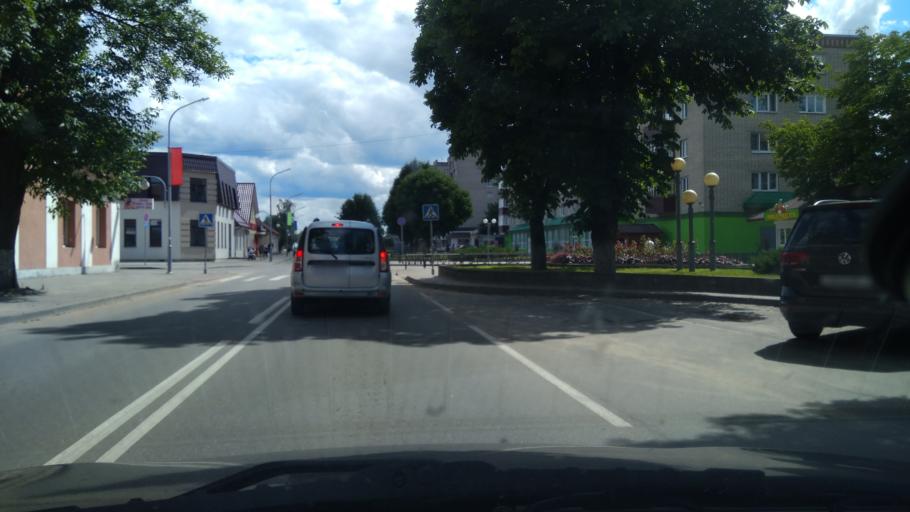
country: BY
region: Grodnenskaya
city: Shchuchin
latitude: 53.6033
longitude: 24.7420
